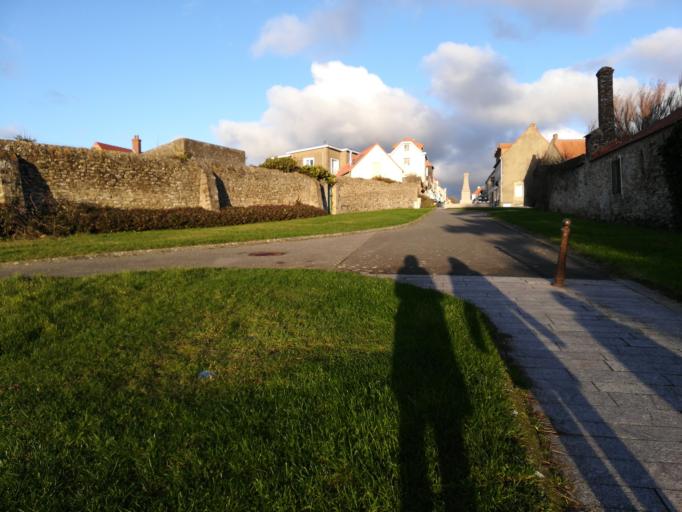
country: FR
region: Nord-Pas-de-Calais
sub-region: Departement du Pas-de-Calais
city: Ambleteuse
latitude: 50.8084
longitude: 1.6054
